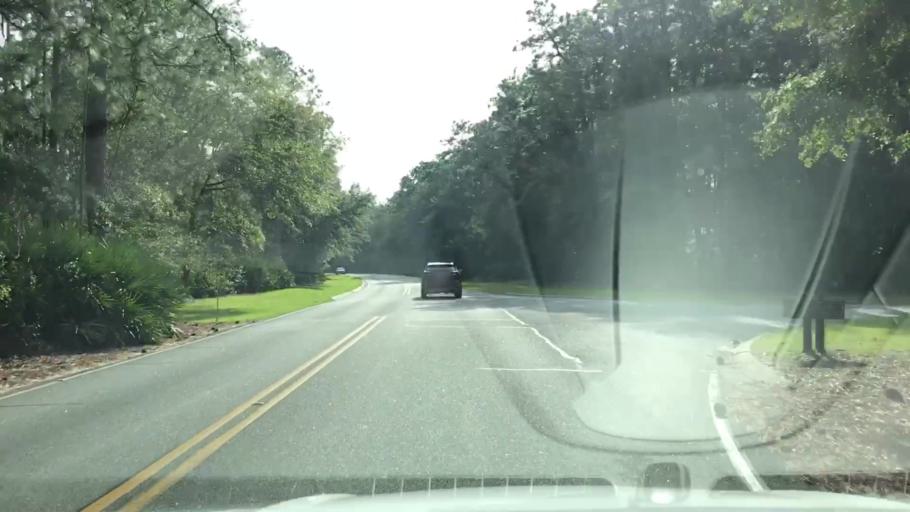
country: US
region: South Carolina
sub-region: Beaufort County
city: Hilton Head Island
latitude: 32.2343
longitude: -80.7246
